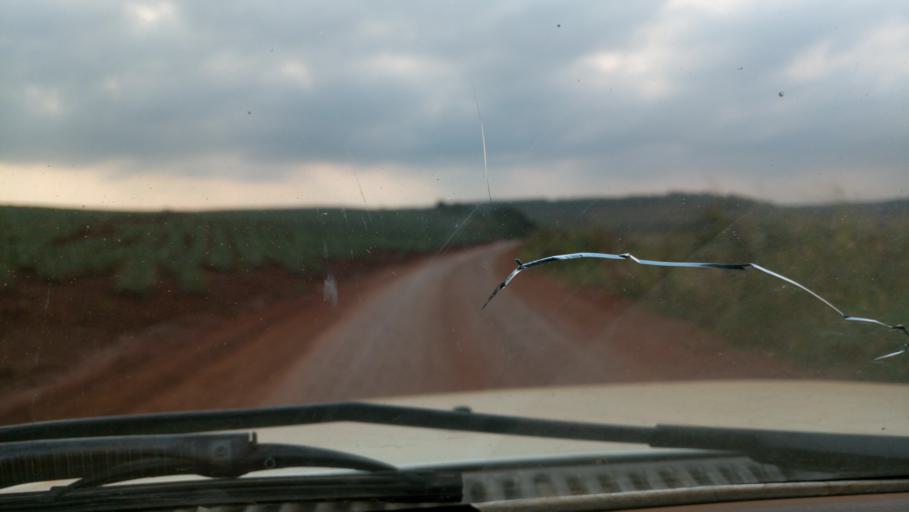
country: KE
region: Nairobi Area
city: Thika
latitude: -1.0003
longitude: 37.1178
